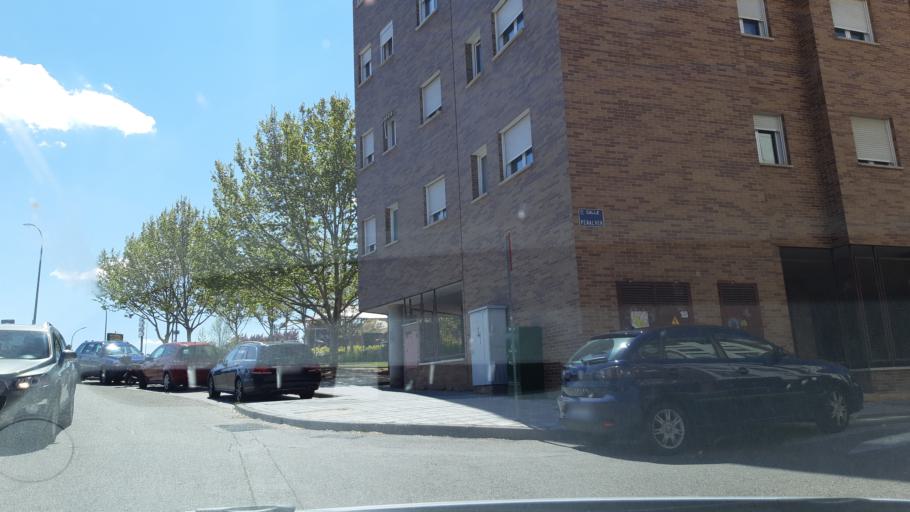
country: ES
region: Castille-La Mancha
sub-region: Provincia de Guadalajara
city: Guadalajara
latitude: 40.6314
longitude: -3.1494
